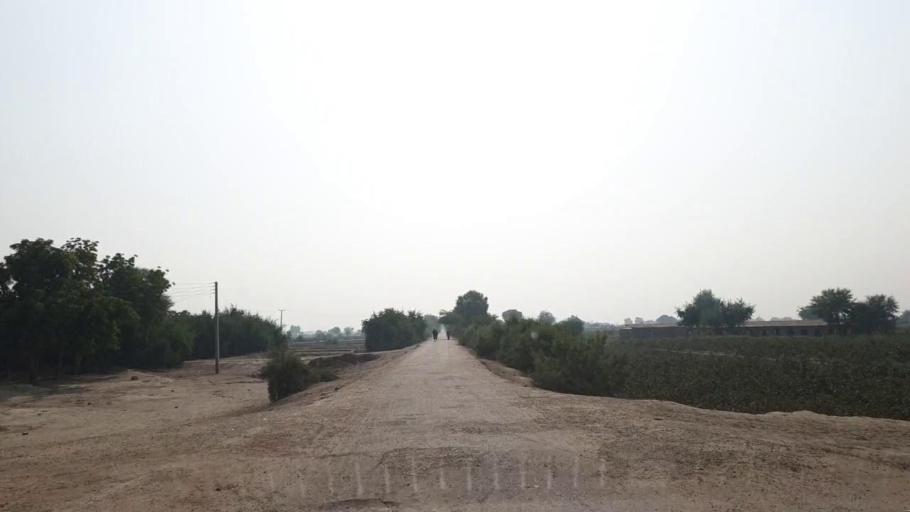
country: PK
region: Sindh
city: Bhan
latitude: 26.4790
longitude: 67.7712
